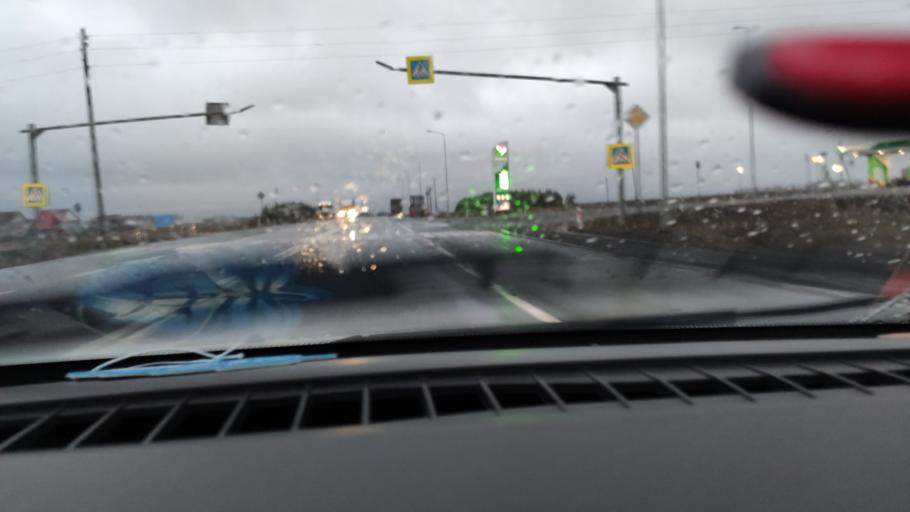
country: RU
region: Udmurtiya
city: Alnashi
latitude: 56.1716
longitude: 52.4743
